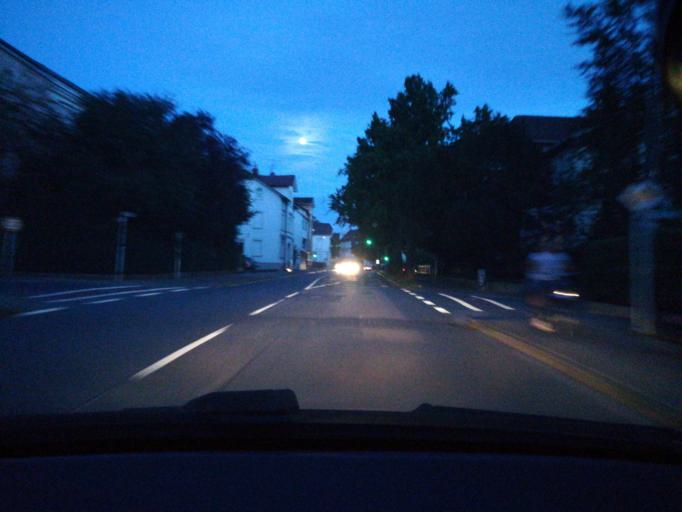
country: DE
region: North Rhine-Westphalia
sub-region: Regierungsbezirk Detmold
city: Minden
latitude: 52.2957
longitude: 8.9126
